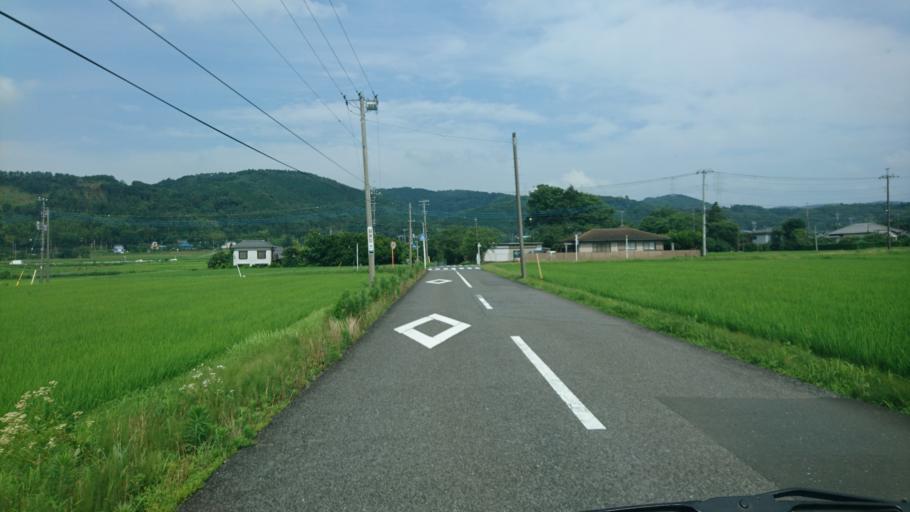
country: JP
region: Chiba
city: Kimitsu
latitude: 35.2931
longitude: 139.9860
